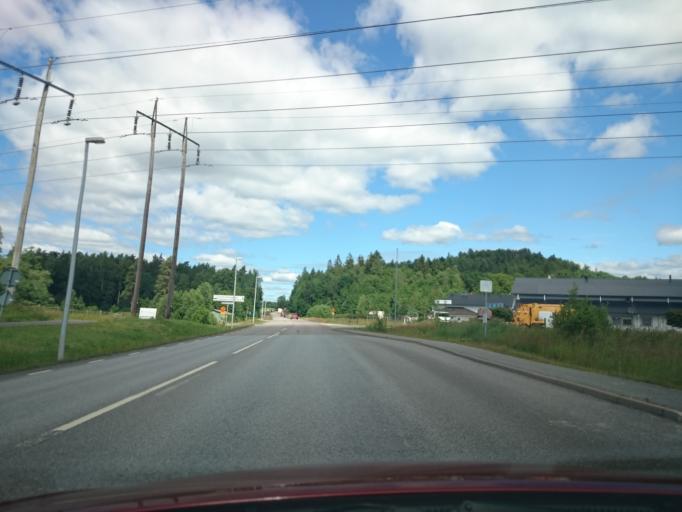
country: SE
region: Vaestra Goetaland
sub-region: Lerums Kommun
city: Stenkullen
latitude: 57.8045
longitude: 12.3057
